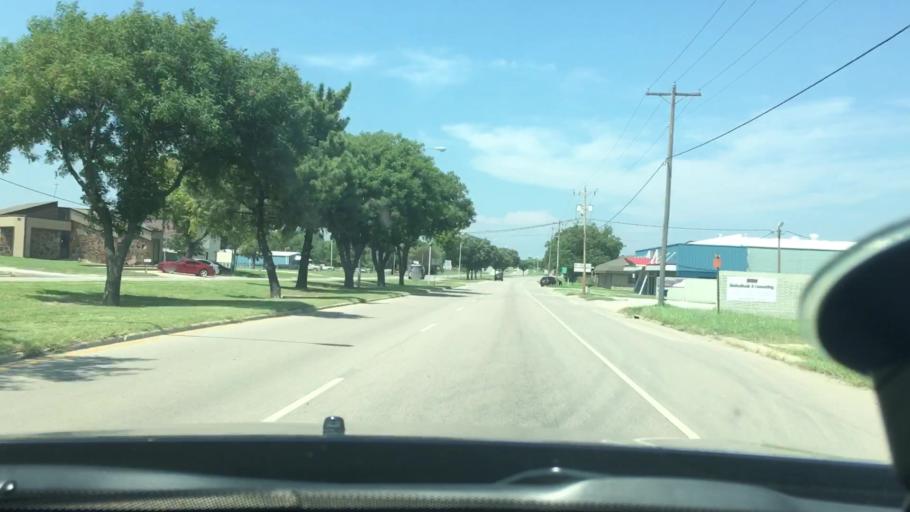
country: US
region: Oklahoma
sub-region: Pontotoc County
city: Ada
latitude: 34.7968
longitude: -96.6786
